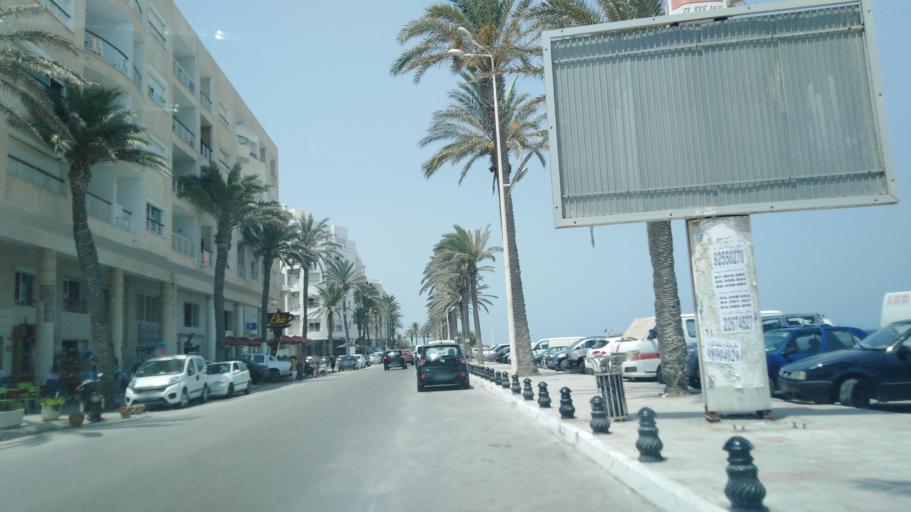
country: TN
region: Al Mahdiyah
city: Mahdia
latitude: 35.5209
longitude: 11.0426
